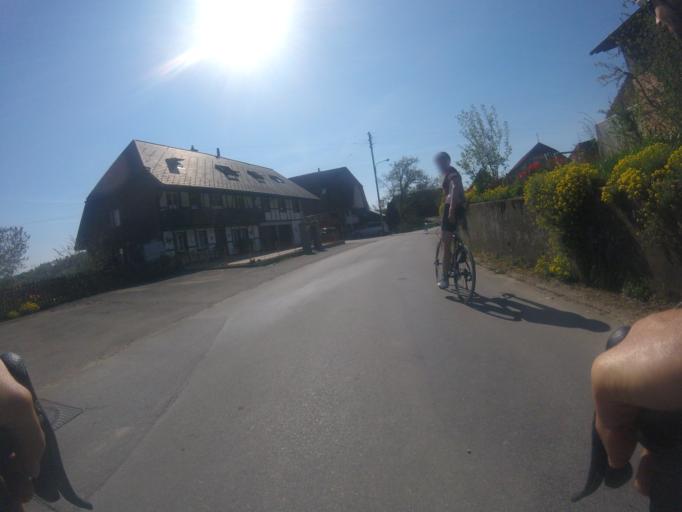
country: CH
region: Bern
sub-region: Bern-Mittelland District
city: Muhleberg
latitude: 46.9703
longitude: 7.2404
